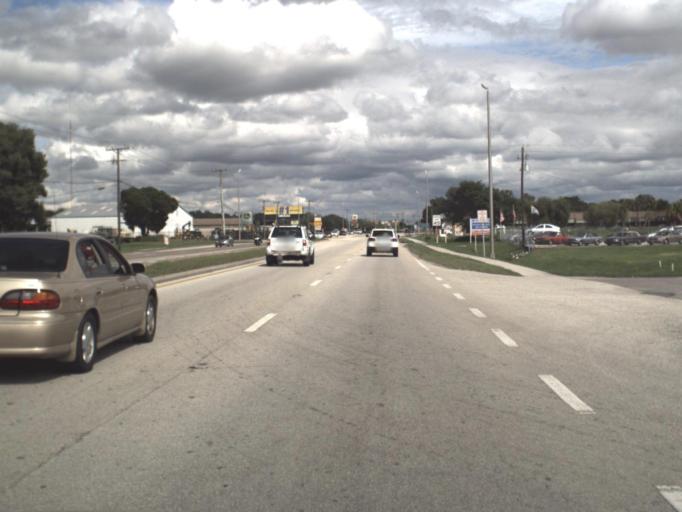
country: US
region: Florida
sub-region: Manatee County
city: Palmetto
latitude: 27.5212
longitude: -82.5575
